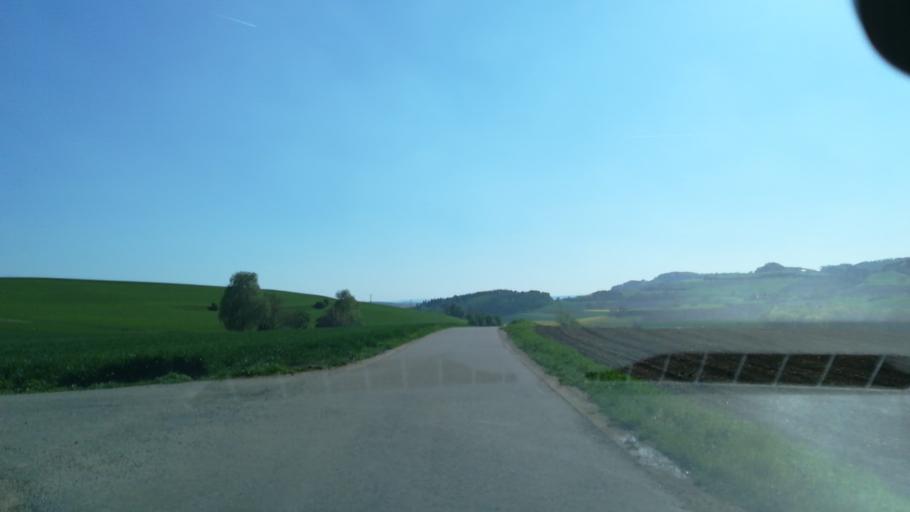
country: DE
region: Baden-Wuerttemberg
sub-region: Freiburg Region
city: Muhlhausen-Ehingen
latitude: 47.8010
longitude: 8.7973
